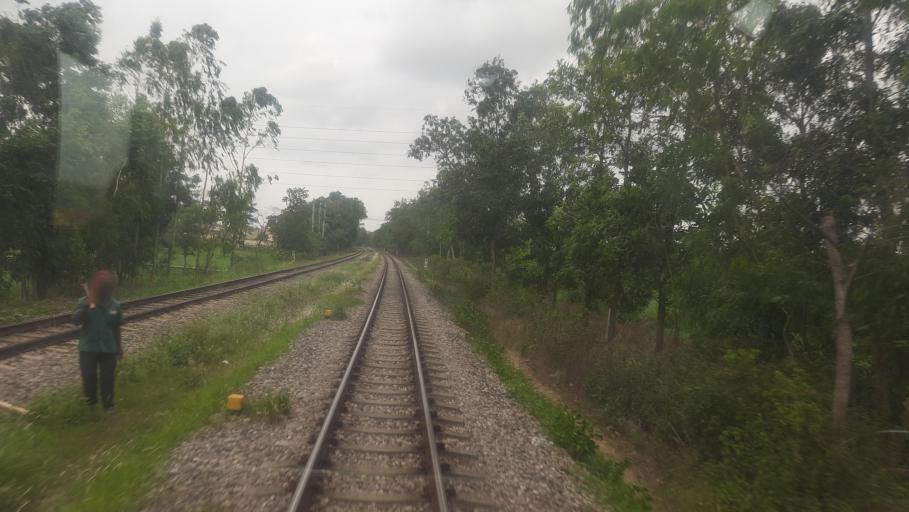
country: BD
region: Chittagong
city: Chhagalnaiya
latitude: 22.9090
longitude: 91.5312
